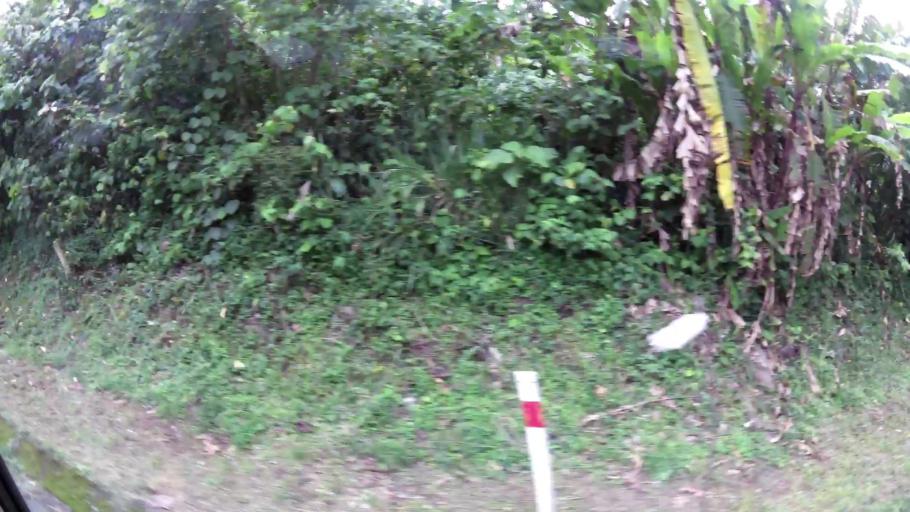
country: EC
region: Santo Domingo de los Tsachilas
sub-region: Canton Santo Domingo de los Colorados
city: Santo Domingo de los Colorados
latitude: -0.2696
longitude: -79.0835
